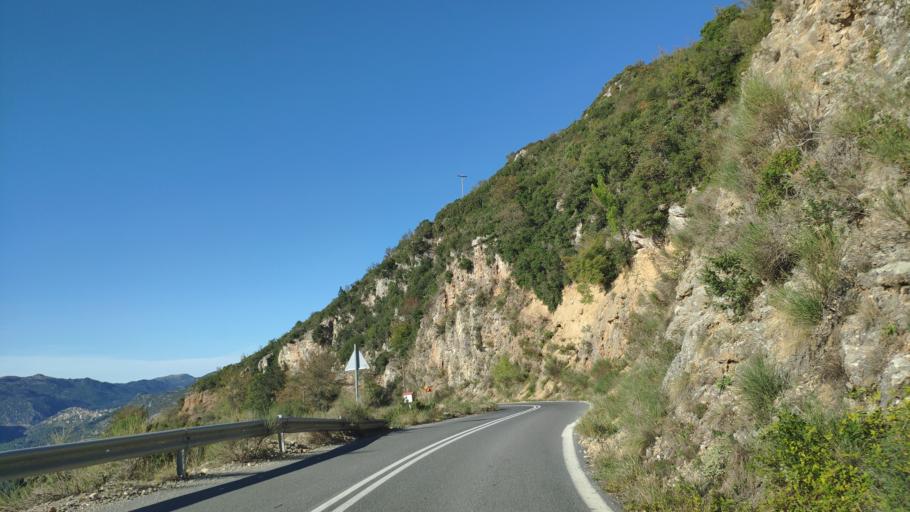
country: GR
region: Peloponnese
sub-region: Nomos Arkadias
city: Dimitsana
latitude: 37.5518
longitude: 22.0647
